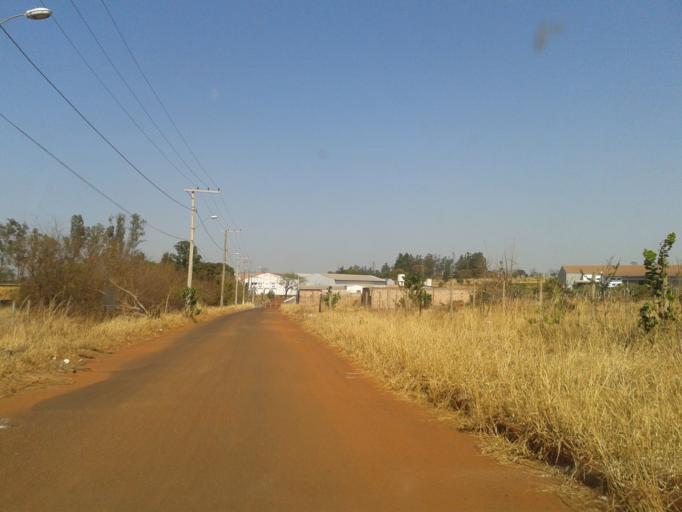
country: BR
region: Minas Gerais
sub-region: Ituiutaba
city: Ituiutaba
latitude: -18.9614
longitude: -49.4888
